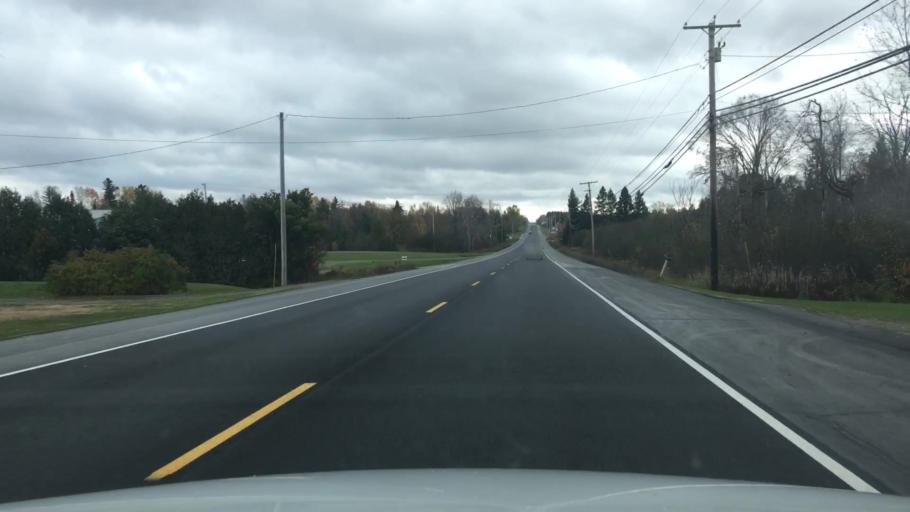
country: US
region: Maine
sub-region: Aroostook County
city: Houlton
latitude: 46.2466
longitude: -67.8408
